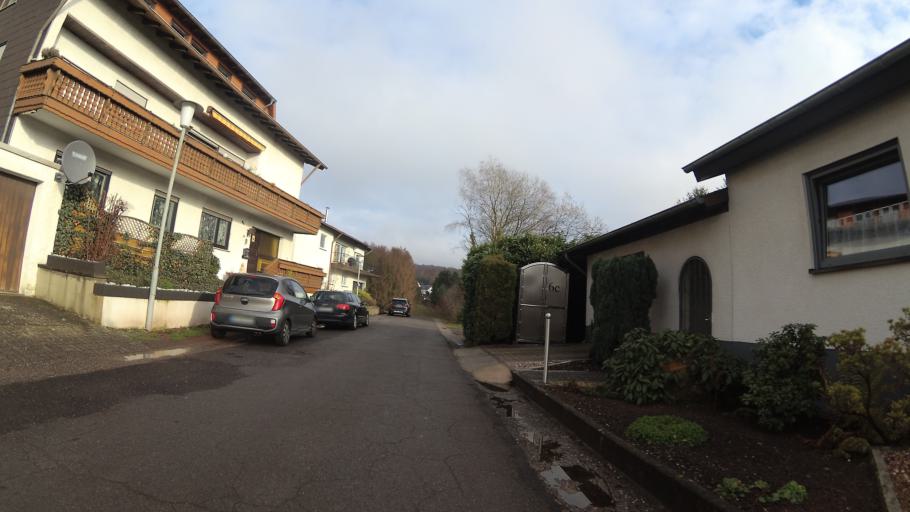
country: DE
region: Saarland
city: Spiesen-Elversberg
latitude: 49.3201
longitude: 7.1556
